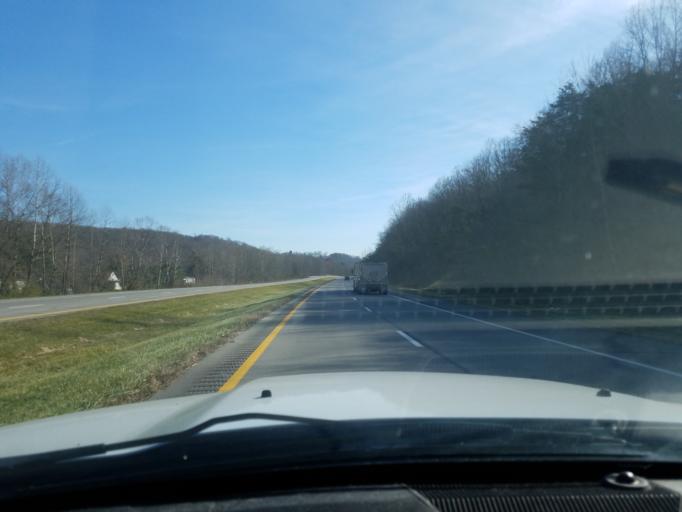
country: US
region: Ohio
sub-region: Pike County
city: Piketon
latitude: 39.0593
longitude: -83.0730
